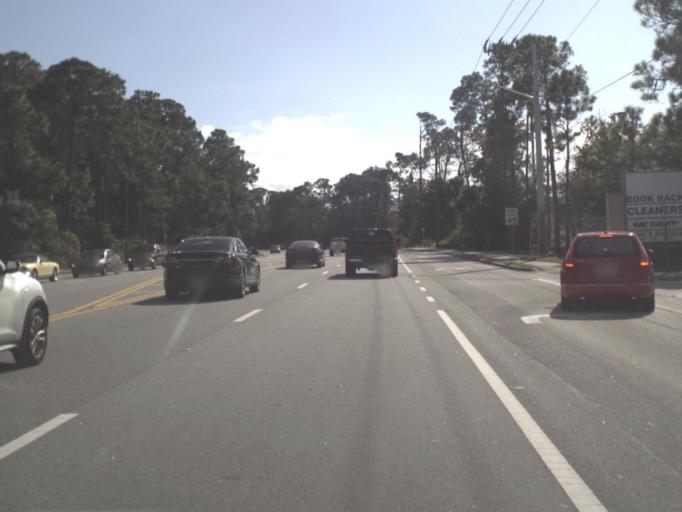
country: US
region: Florida
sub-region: Volusia County
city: South Daytona
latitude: 29.1426
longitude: -81.0353
